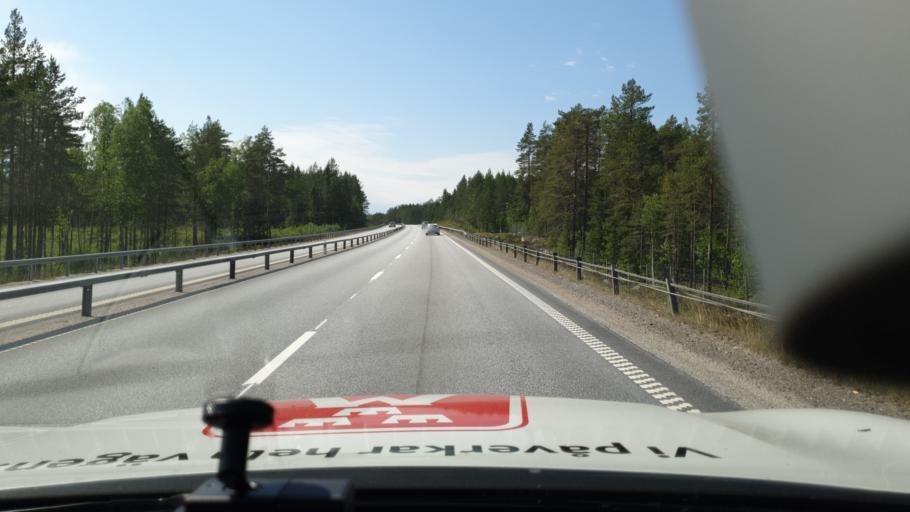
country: SE
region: Vaesterbotten
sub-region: Umea Kommun
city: Hoernefors
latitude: 63.6114
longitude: 19.7920
